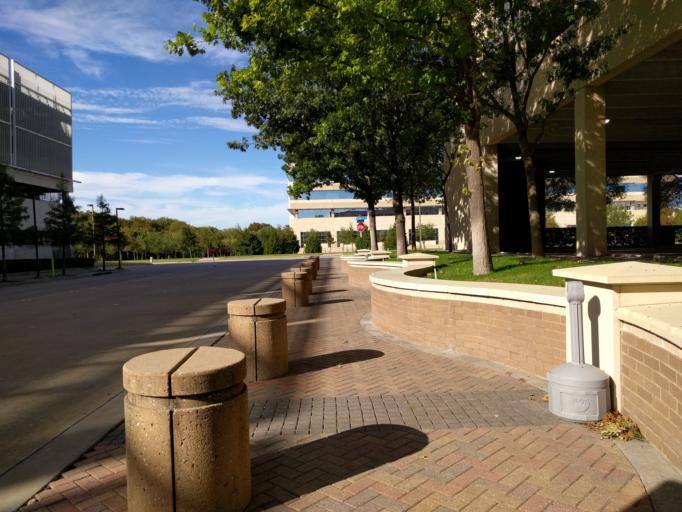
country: US
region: Texas
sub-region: Collin County
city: Plano
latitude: 32.9861
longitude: -96.7084
